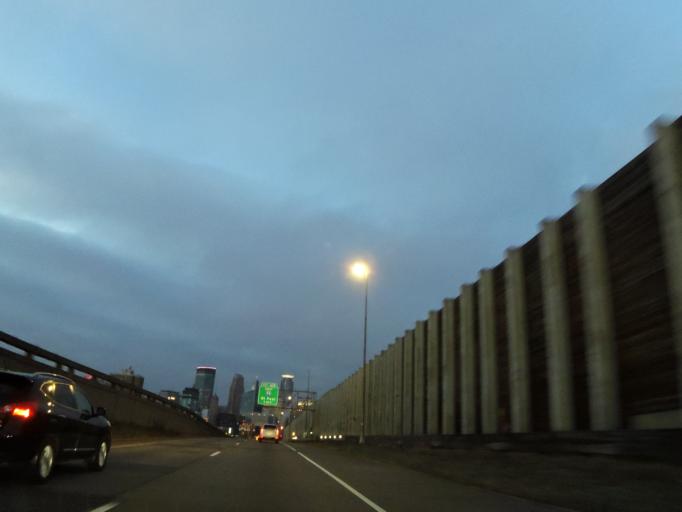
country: US
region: Minnesota
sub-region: Hennepin County
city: Minneapolis
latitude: 44.9595
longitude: -93.2691
